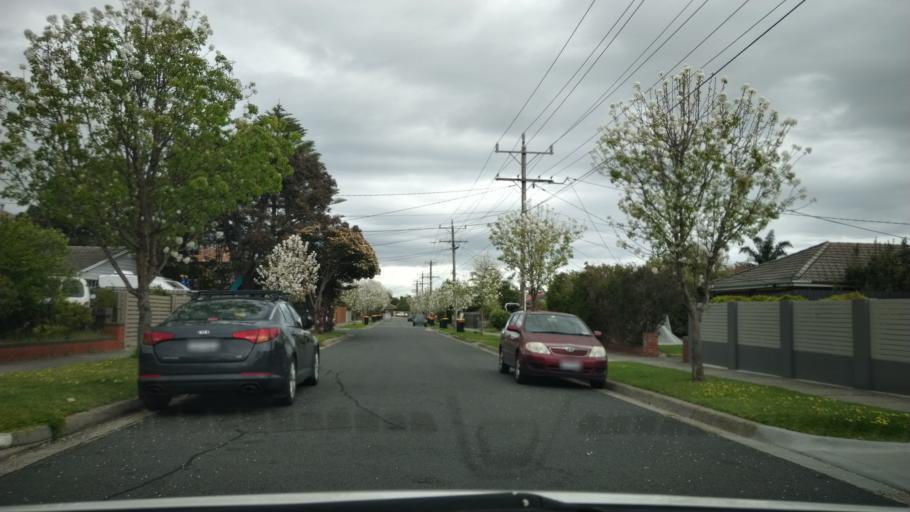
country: AU
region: Victoria
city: Heatherton
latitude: -37.9655
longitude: 145.0786
